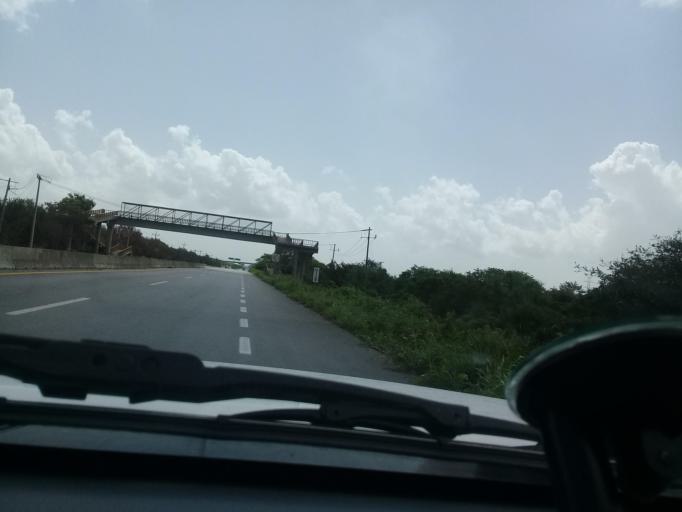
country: MX
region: Veracruz
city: Moralillo
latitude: 22.2125
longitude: -97.9573
